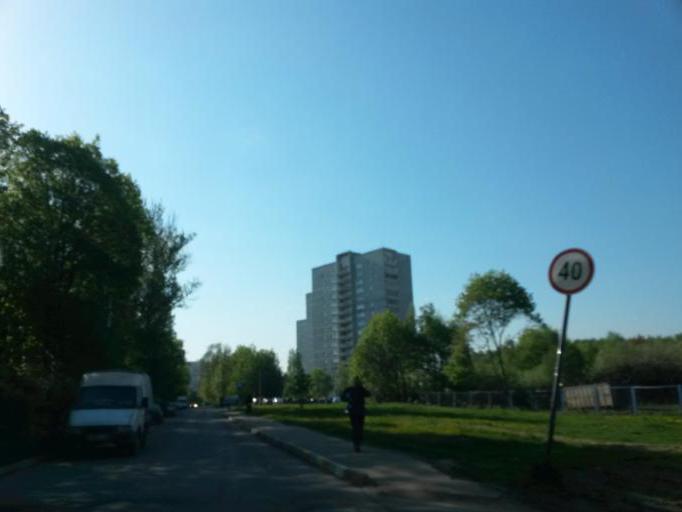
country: RU
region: Moskovskaya
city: Razvilka
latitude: 55.5910
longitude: 37.7501
